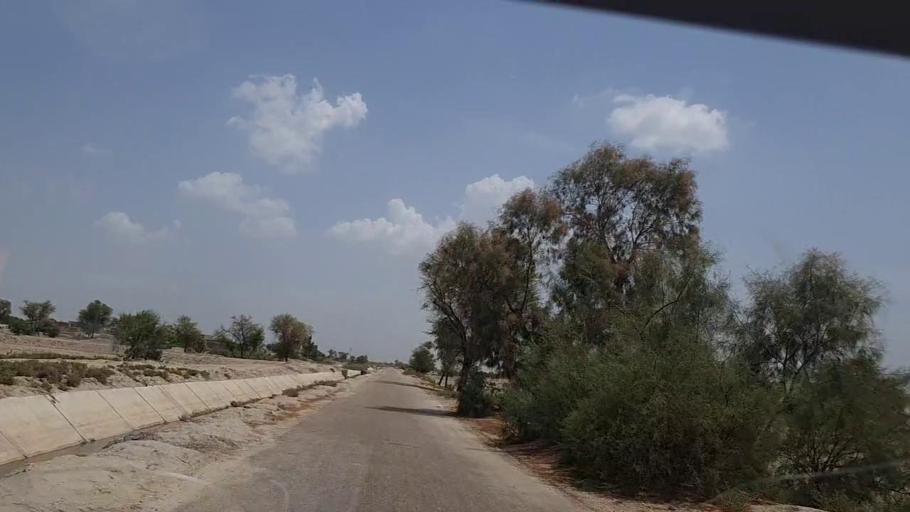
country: PK
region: Sindh
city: Bhan
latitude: 26.5319
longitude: 67.6326
